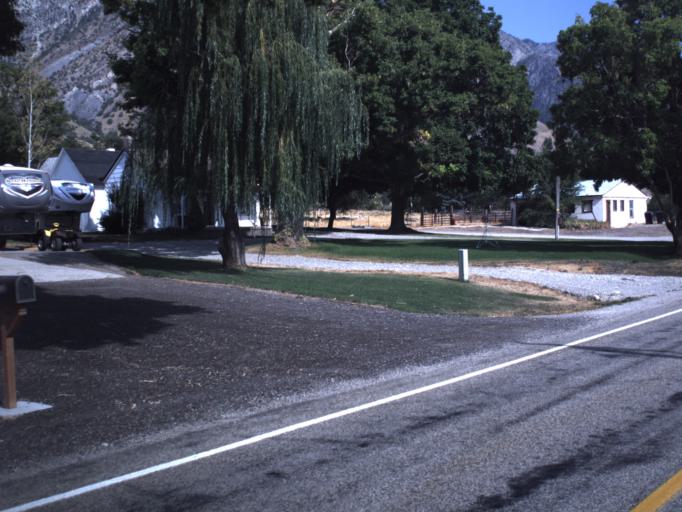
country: US
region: Utah
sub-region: Box Elder County
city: Honeyville
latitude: 41.6051
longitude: -112.0574
